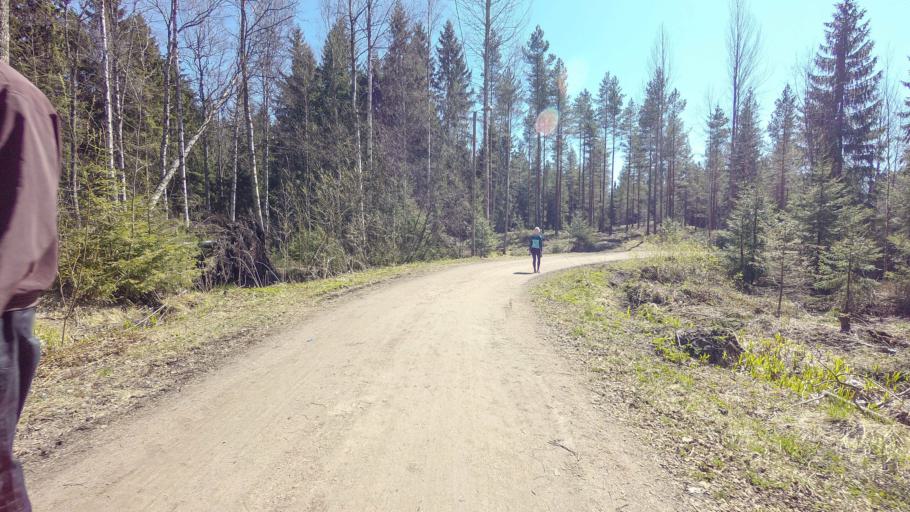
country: FI
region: Uusimaa
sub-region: Helsinki
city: Vantaa
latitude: 60.2266
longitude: 25.1474
